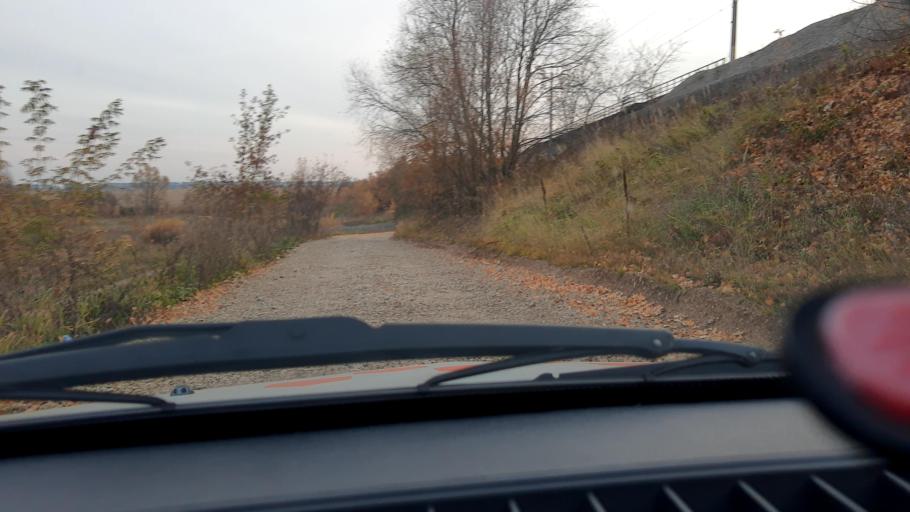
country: RU
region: Bashkortostan
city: Iglino
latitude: 54.7924
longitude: 56.3338
